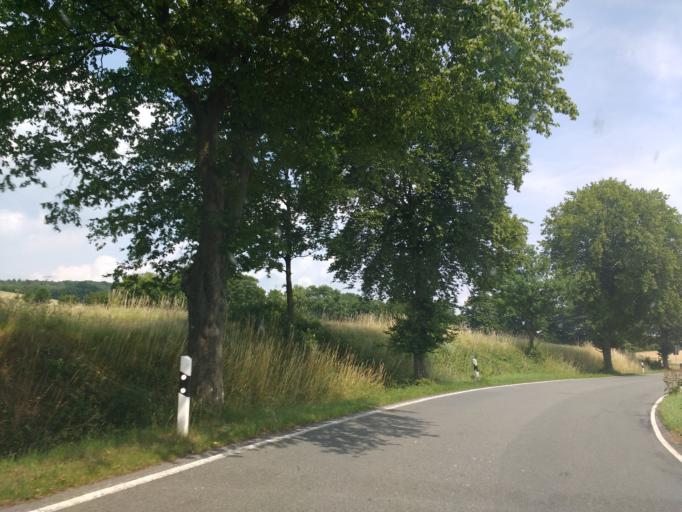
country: DE
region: North Rhine-Westphalia
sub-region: Regierungsbezirk Detmold
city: Dorentrup
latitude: 52.0640
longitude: 9.0154
